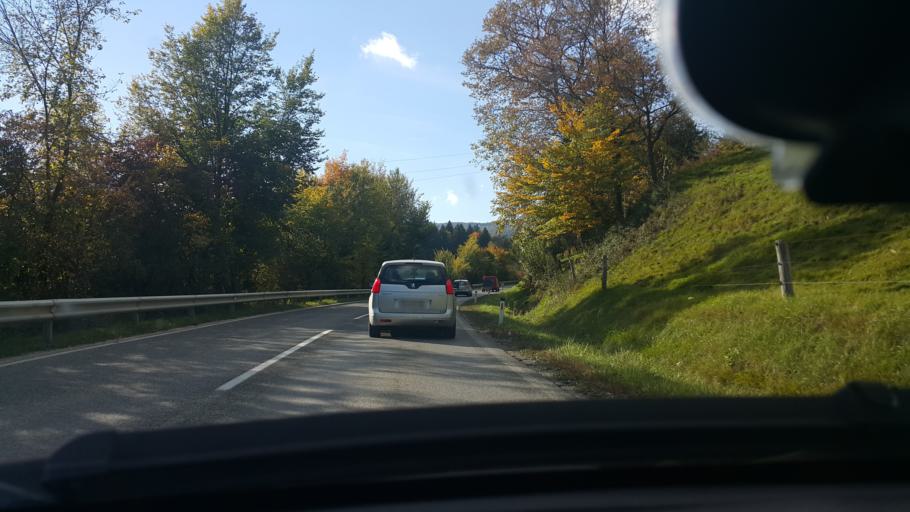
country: SI
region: Zrece
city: Zrece
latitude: 46.3582
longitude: 15.3795
